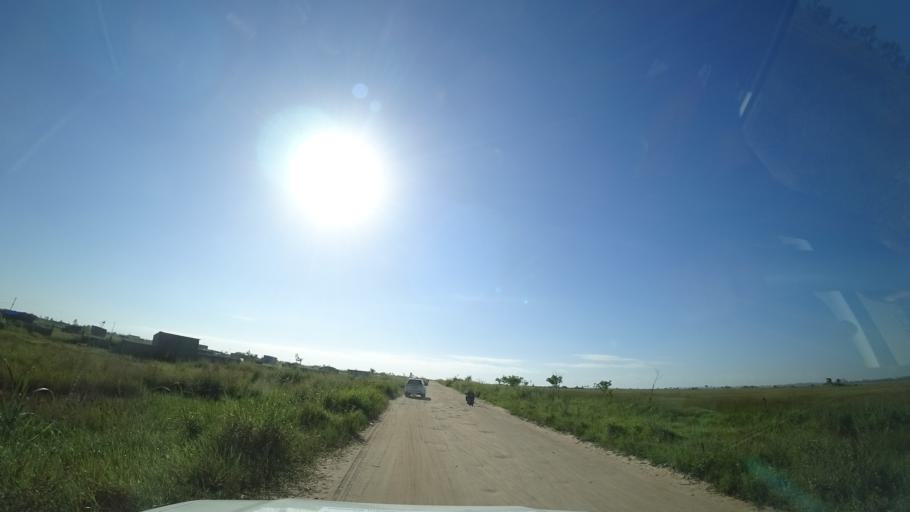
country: MZ
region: Sofala
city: Beira
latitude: -19.7635
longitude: 34.9024
